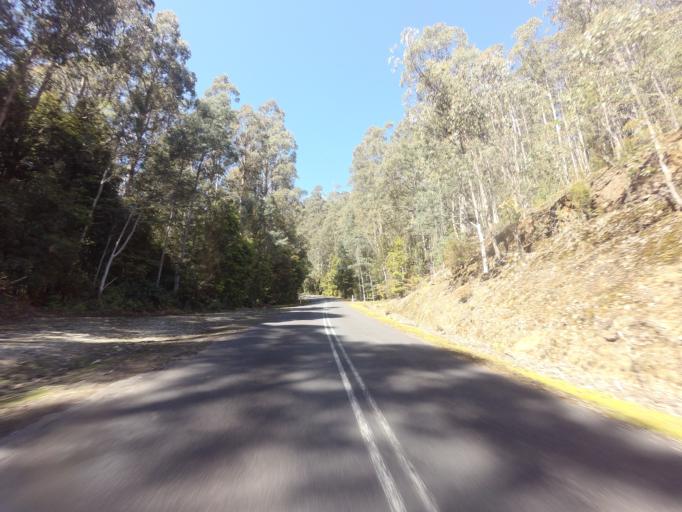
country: AU
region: Tasmania
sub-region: Huon Valley
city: Geeveston
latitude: -42.8190
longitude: 146.3427
